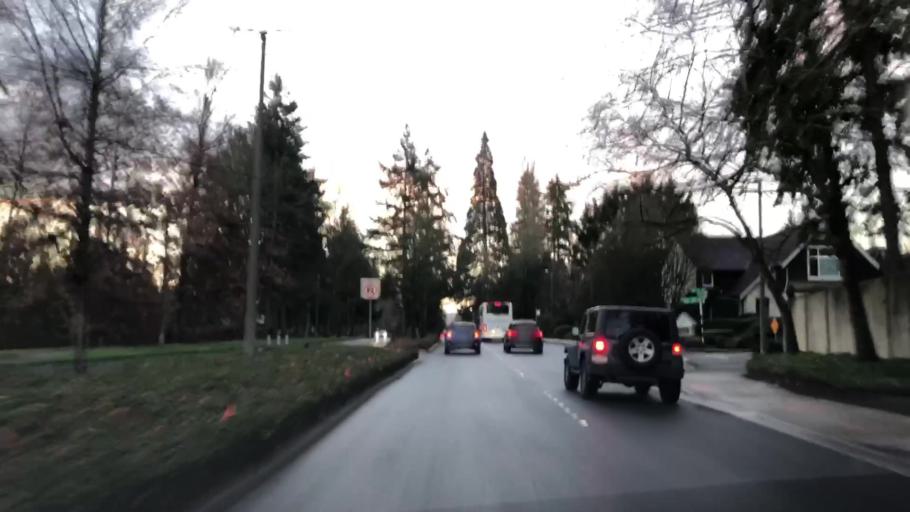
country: US
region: Washington
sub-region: King County
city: Eastgate
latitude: 47.6252
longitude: -122.1432
